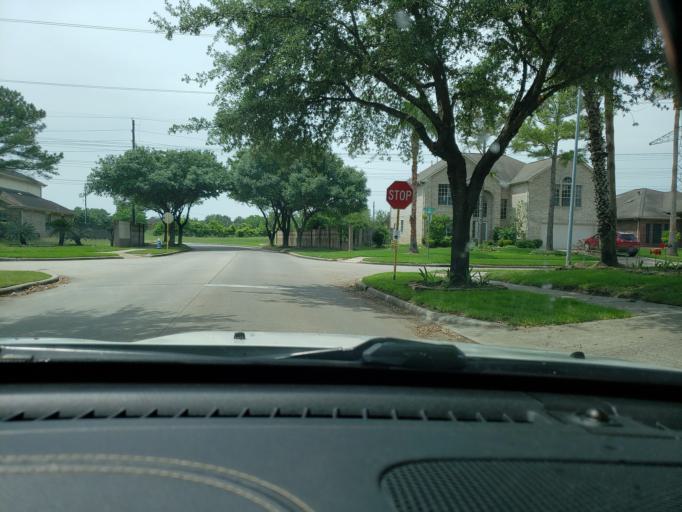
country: US
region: Texas
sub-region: Harris County
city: Jersey Village
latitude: 29.9200
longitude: -95.5770
